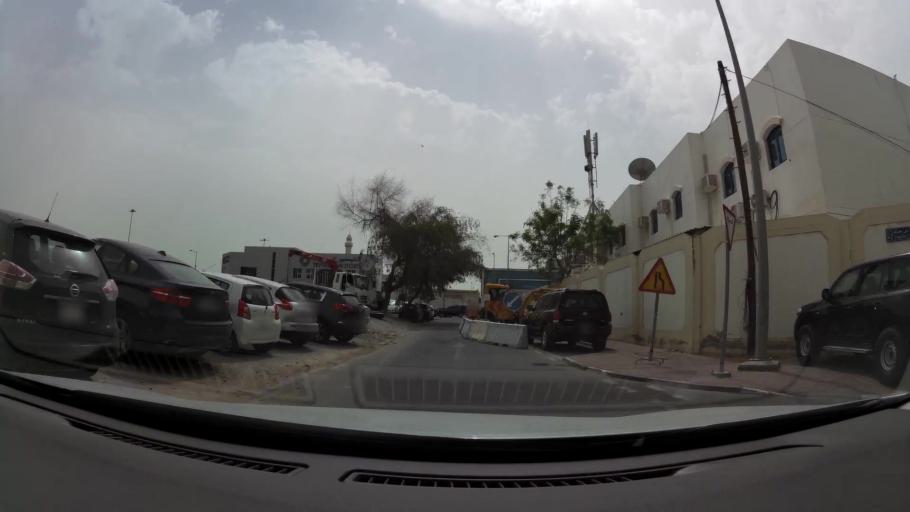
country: QA
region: Baladiyat ad Dawhah
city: Doha
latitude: 25.2648
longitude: 51.5533
